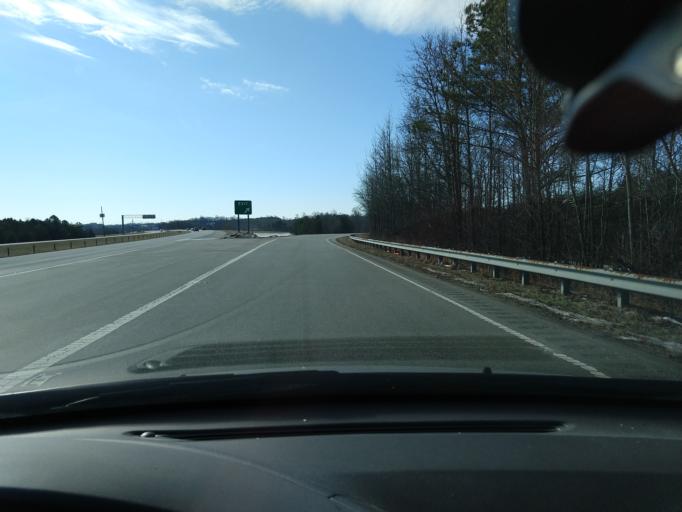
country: US
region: North Carolina
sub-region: Guilford County
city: Oak Ridge
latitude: 36.0991
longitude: -79.9667
